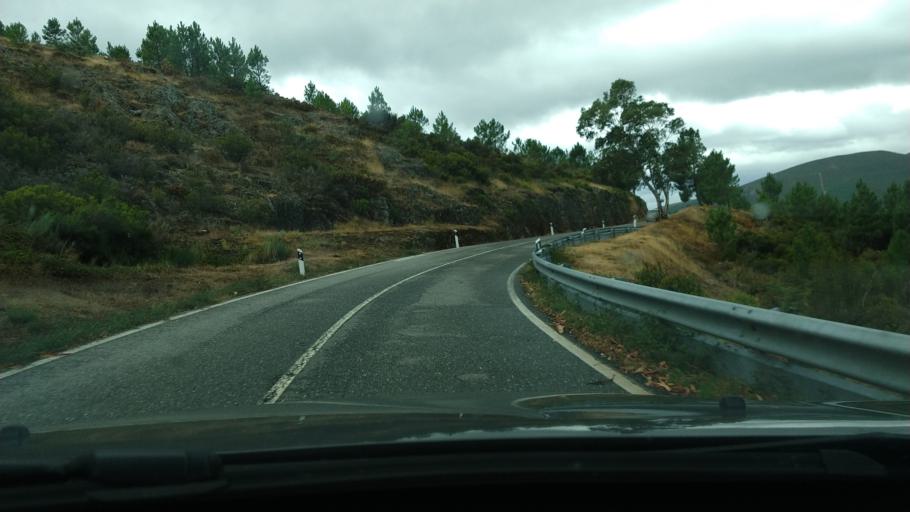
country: PT
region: Castelo Branco
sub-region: Covilha
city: Covilha
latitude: 40.2389
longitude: -7.6745
